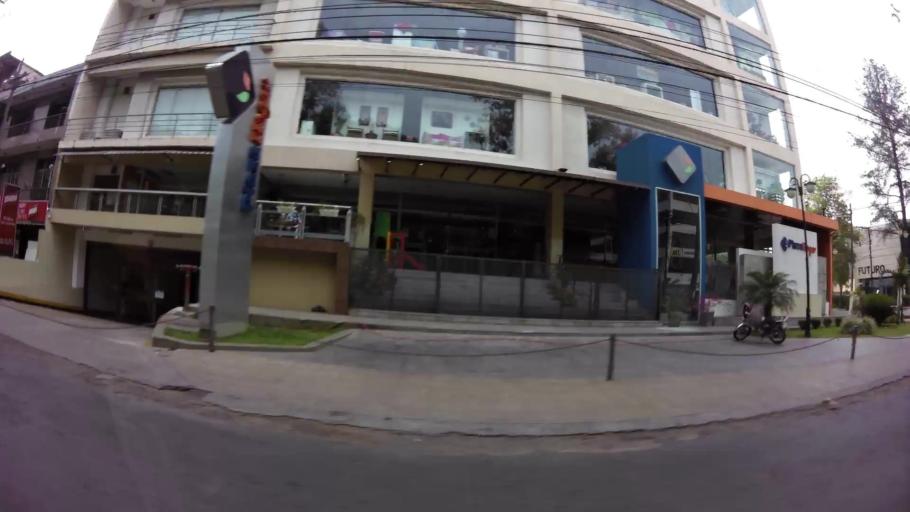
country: PY
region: Asuncion
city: Asuncion
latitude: -25.2911
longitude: -57.5746
